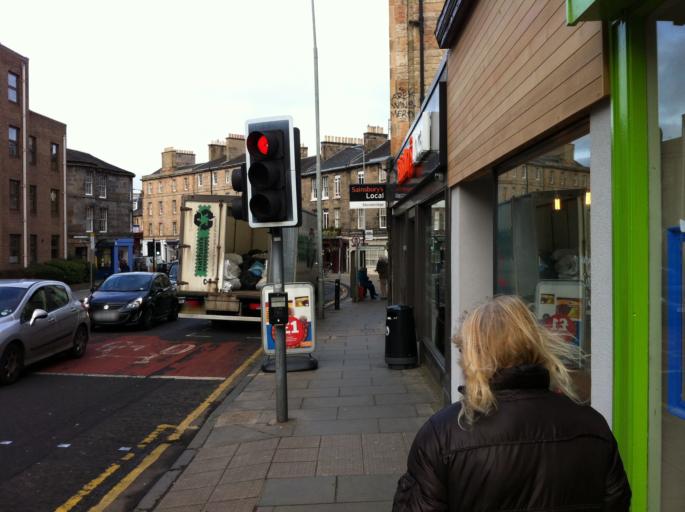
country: GB
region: Scotland
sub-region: Edinburgh
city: Edinburgh
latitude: 55.9585
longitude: -3.2095
